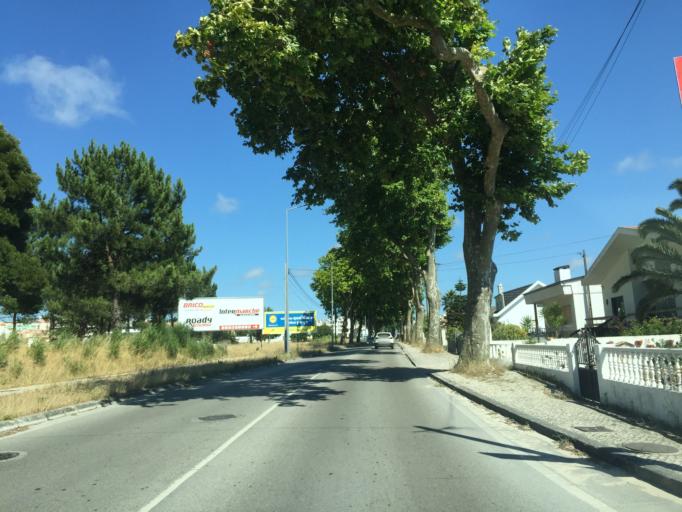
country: PT
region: Leiria
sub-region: Caldas da Rainha
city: Caldas da Rainha
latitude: 39.4062
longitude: -9.1517
